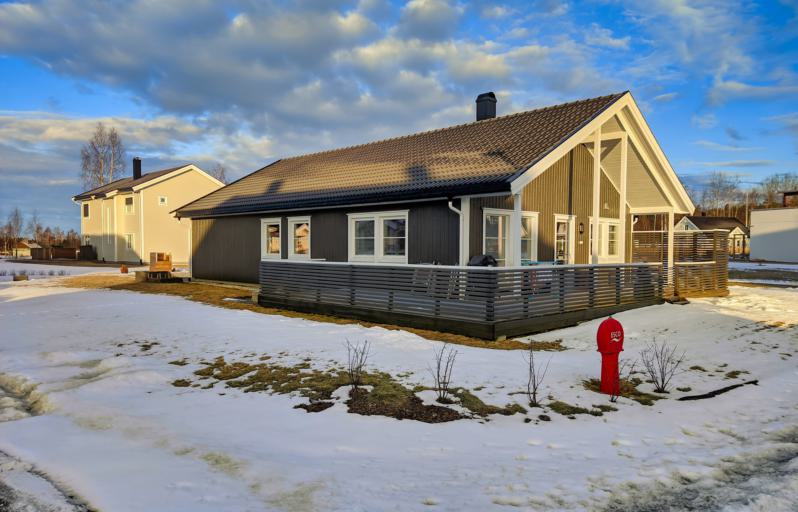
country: NO
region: Akershus
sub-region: Nes
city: Arnes
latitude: 60.1700
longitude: 11.5443
